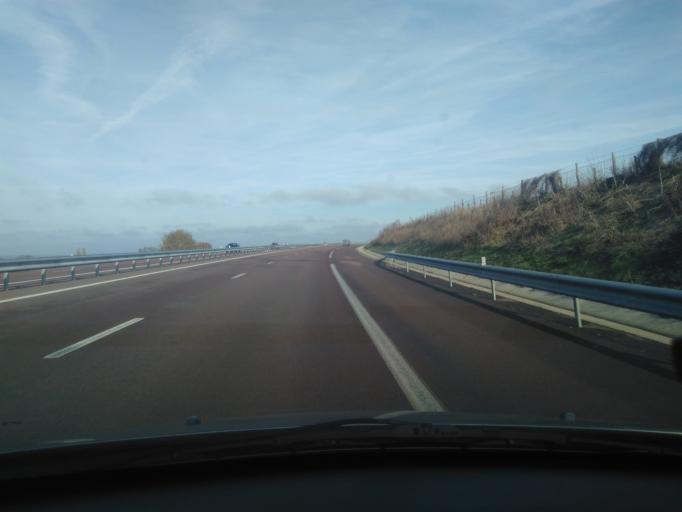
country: FR
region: Bourgogne
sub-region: Departement de la Nievre
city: Magny-Cours
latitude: 46.8413
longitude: 3.1316
